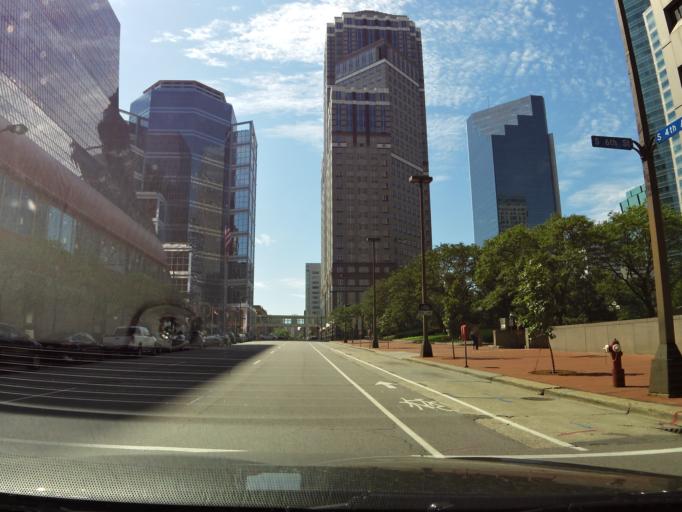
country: US
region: Minnesota
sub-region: Hennepin County
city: Minneapolis
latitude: 44.9755
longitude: -93.2659
